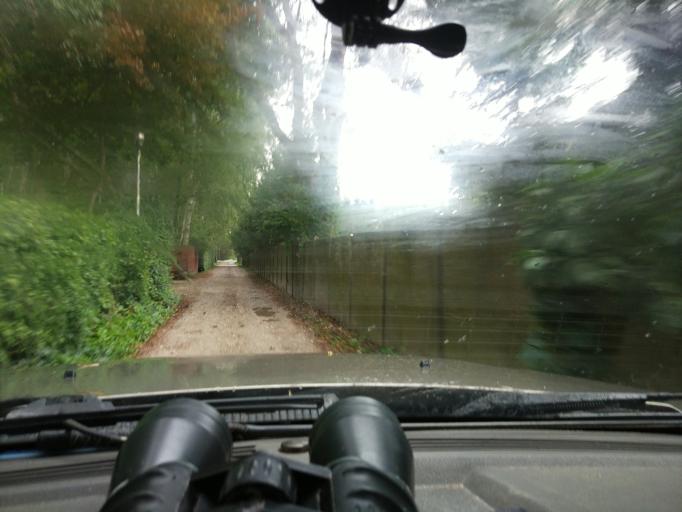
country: PL
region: Masovian Voivodeship
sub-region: Powiat grodziski
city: Podkowa Lesna
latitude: 52.1314
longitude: 20.7358
